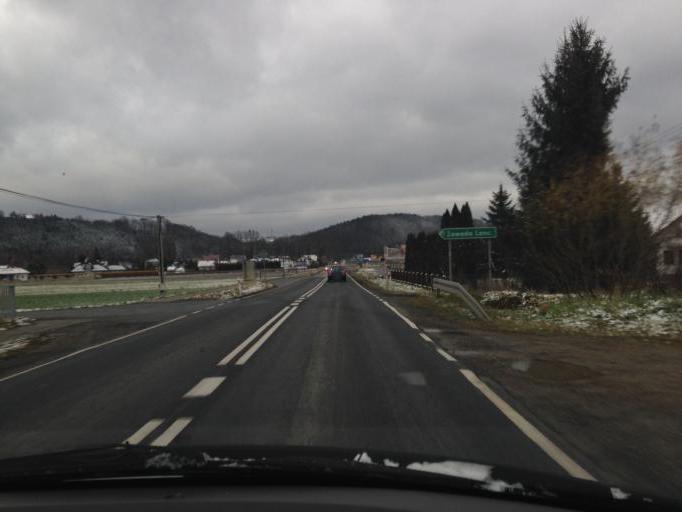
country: PL
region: Lesser Poland Voivodeship
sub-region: Powiat tarnowski
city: Zakliczyn
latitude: 49.8700
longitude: 20.8058
